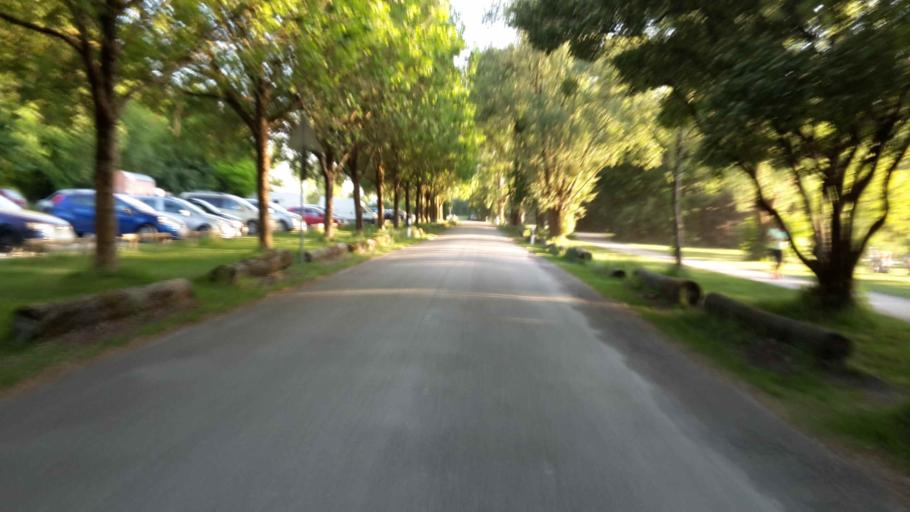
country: DE
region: Bavaria
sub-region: Upper Bavaria
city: Karlsfeld
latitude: 48.2127
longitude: 11.5163
